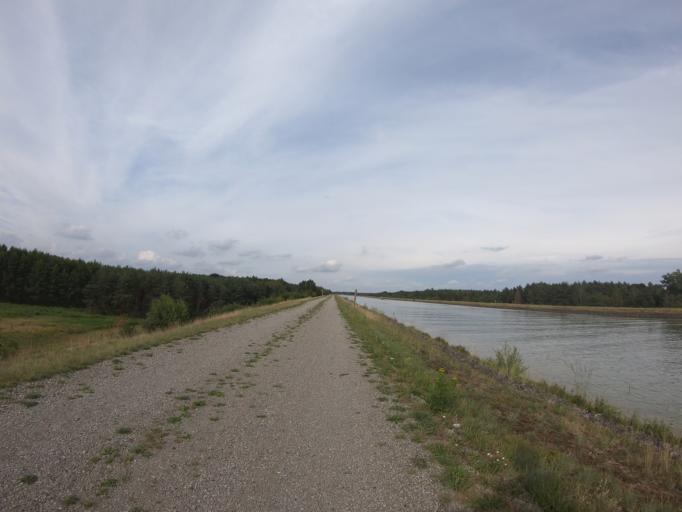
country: DE
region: Lower Saxony
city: Osloss
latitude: 52.4601
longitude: 10.6445
